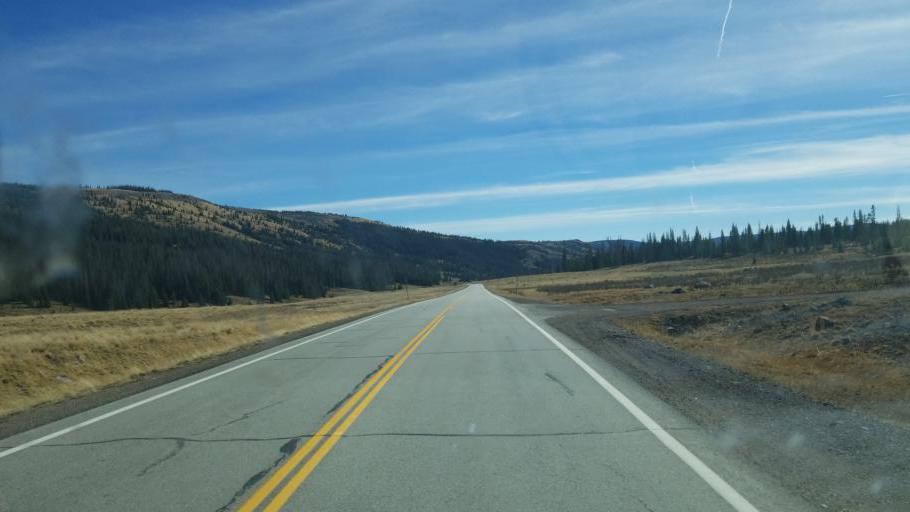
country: US
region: New Mexico
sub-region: Rio Arriba County
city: Chama
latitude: 37.0685
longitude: -106.3972
